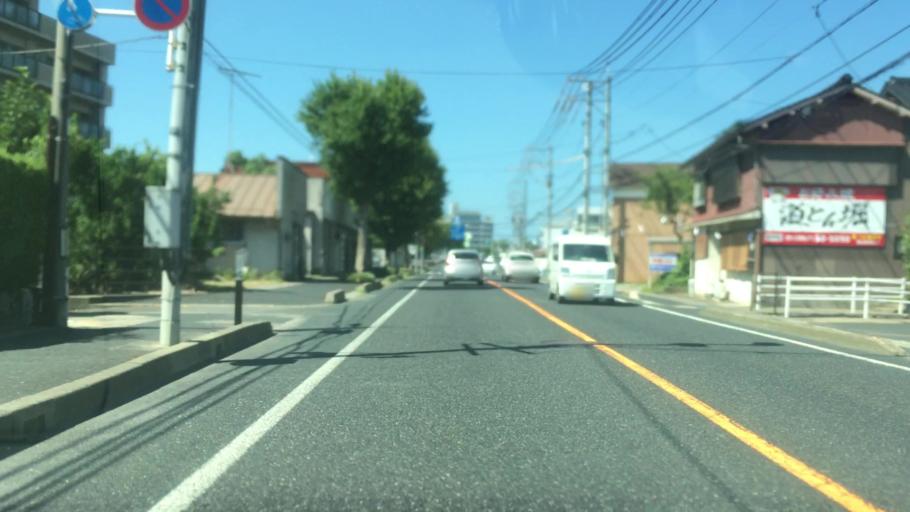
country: JP
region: Tottori
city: Tottori
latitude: 35.4874
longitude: 134.2212
